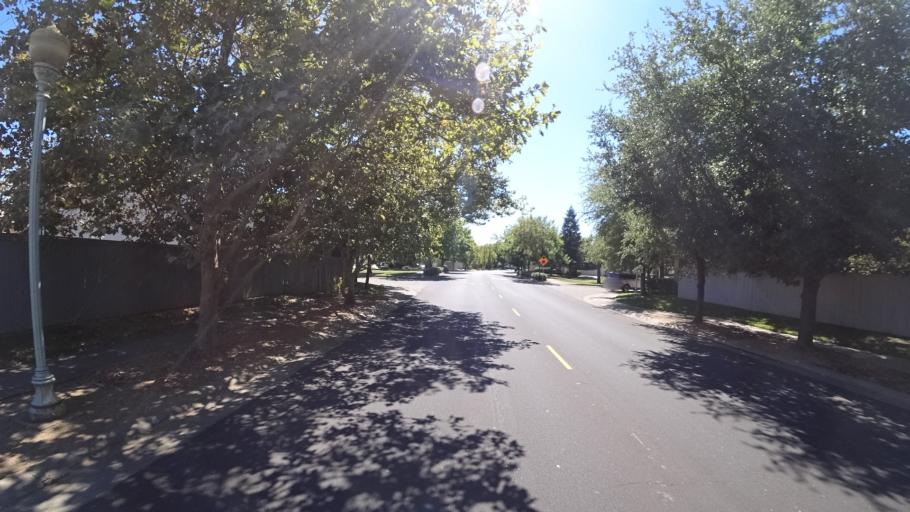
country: US
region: California
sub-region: Sacramento County
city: Laguna
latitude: 38.4199
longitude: -121.4587
